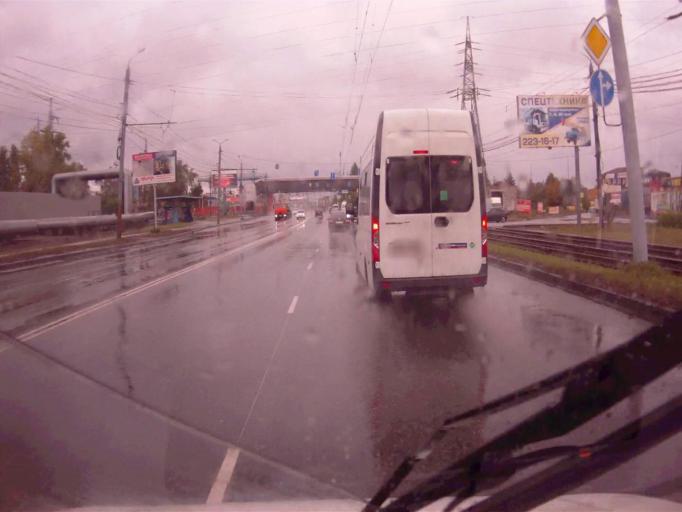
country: RU
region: Chelyabinsk
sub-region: Gorod Chelyabinsk
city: Chelyabinsk
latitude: 55.2038
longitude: 61.3853
